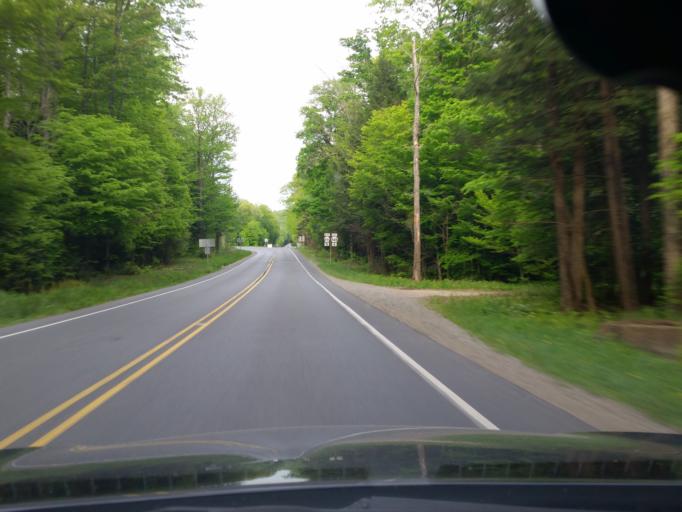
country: US
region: Pennsylvania
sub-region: McKean County
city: Kane
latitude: 41.5706
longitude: -78.8860
